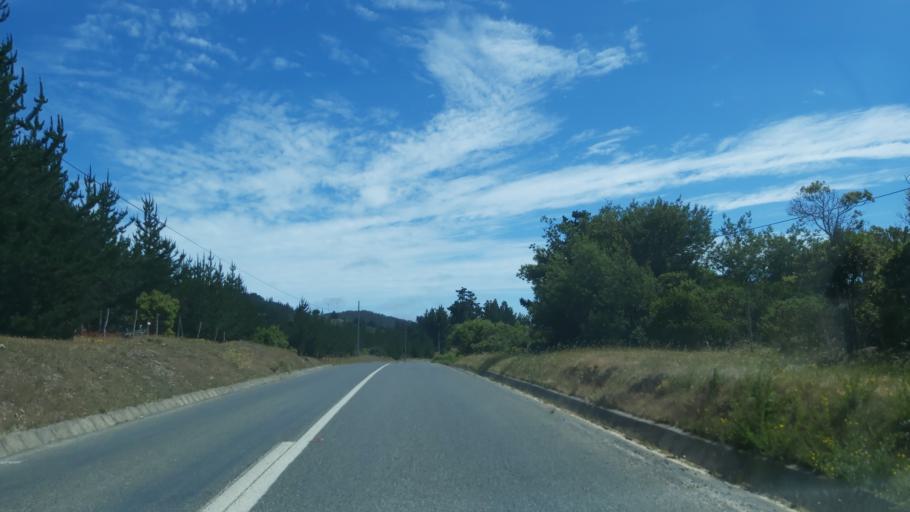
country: CL
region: Maule
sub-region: Provincia de Talca
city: Constitucion
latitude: -35.5574
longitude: -72.5844
